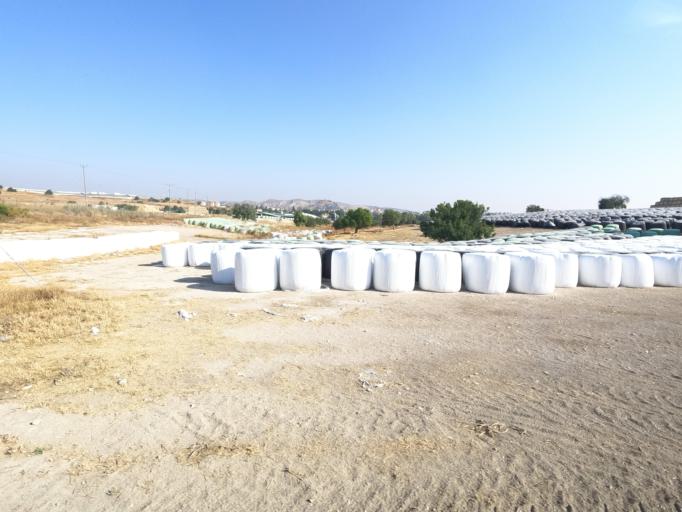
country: CY
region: Lefkosia
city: Lympia
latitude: 34.9853
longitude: 33.4698
